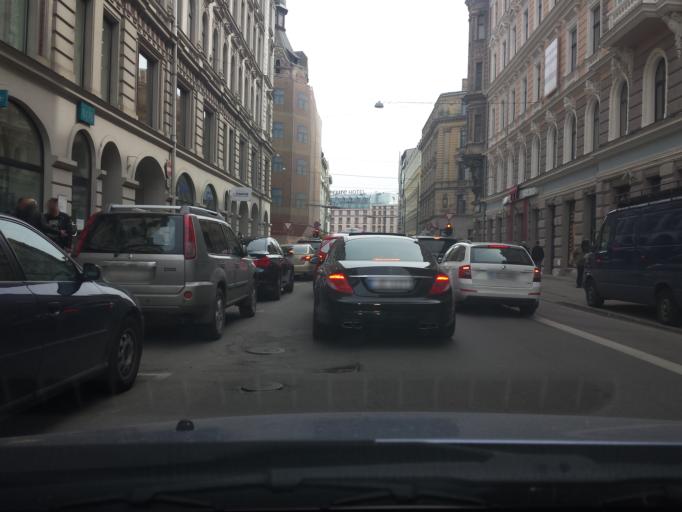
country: LV
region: Riga
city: Riga
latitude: 56.9499
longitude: 24.1221
